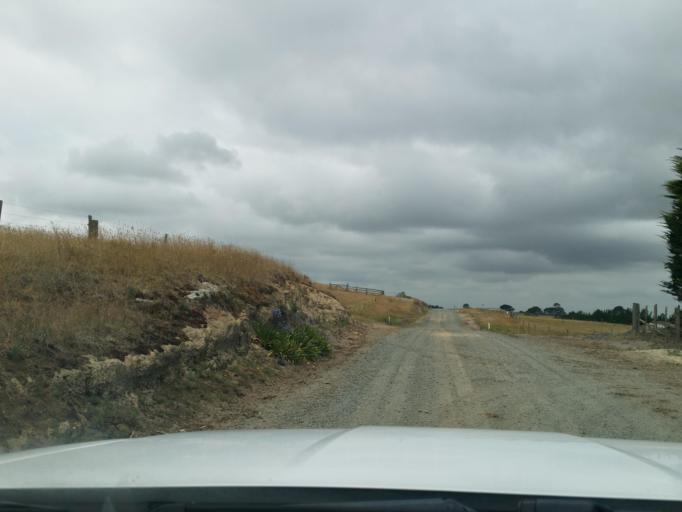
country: NZ
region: Northland
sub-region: Kaipara District
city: Dargaville
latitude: -35.9902
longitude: 173.8283
